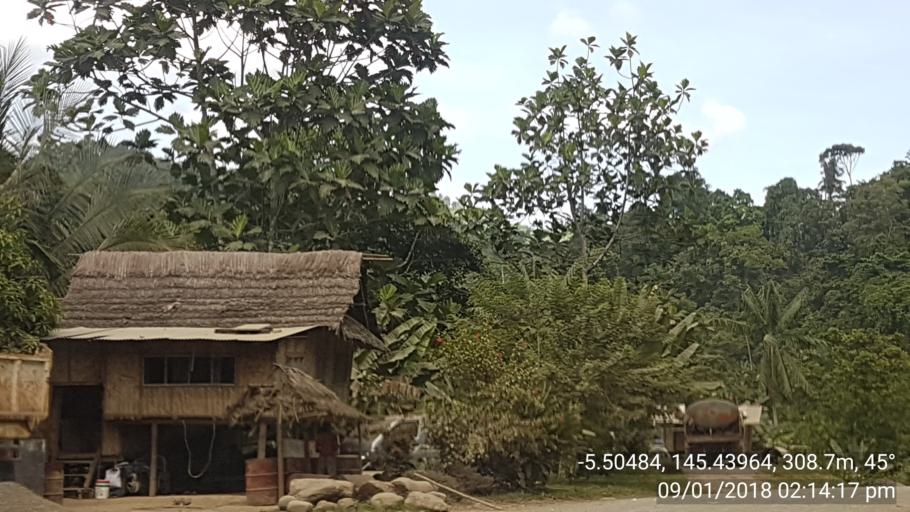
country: PG
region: Madang
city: Madang
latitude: -5.5047
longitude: 145.4397
